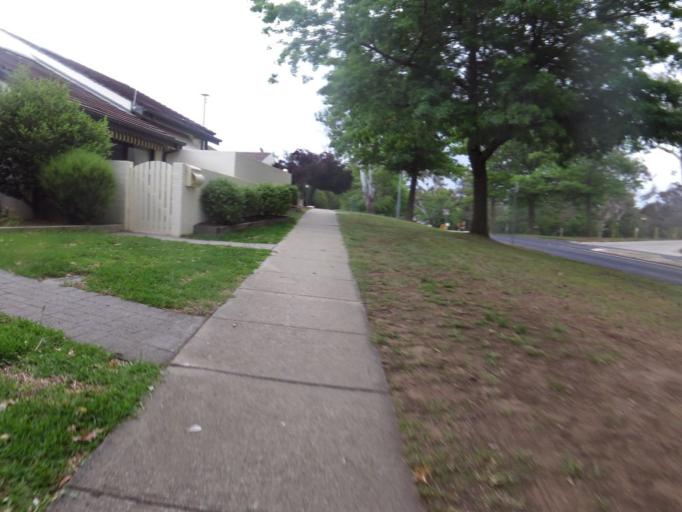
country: AU
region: Australian Capital Territory
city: Forrest
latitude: -35.3401
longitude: 149.1339
